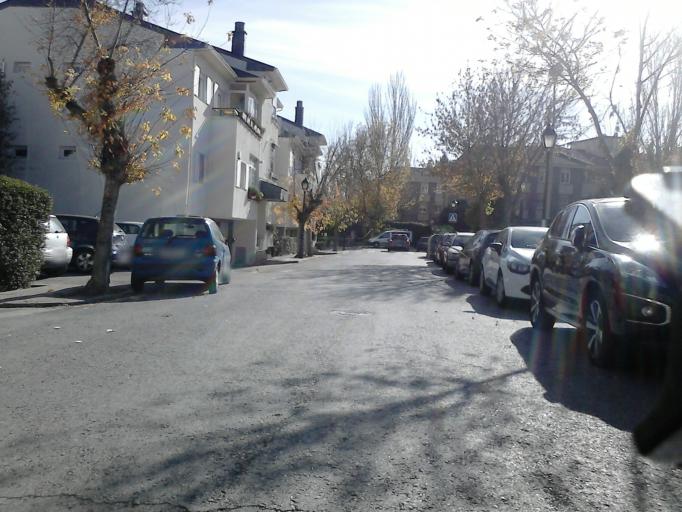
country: ES
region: Madrid
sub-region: Provincia de Madrid
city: Torrelodones
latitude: 40.5783
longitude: -3.9310
